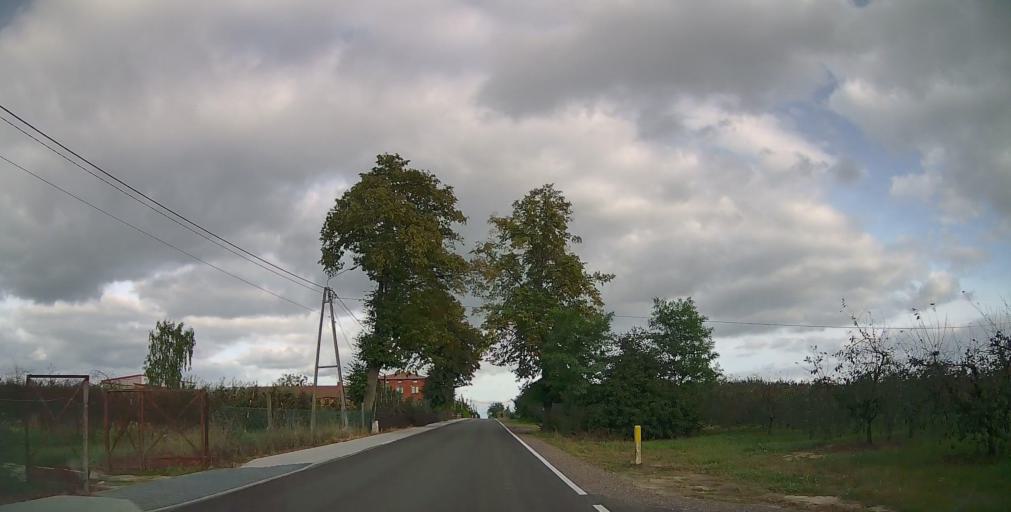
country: PL
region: Masovian Voivodeship
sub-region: Powiat bialobrzeski
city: Promna
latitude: 51.7084
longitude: 20.9382
